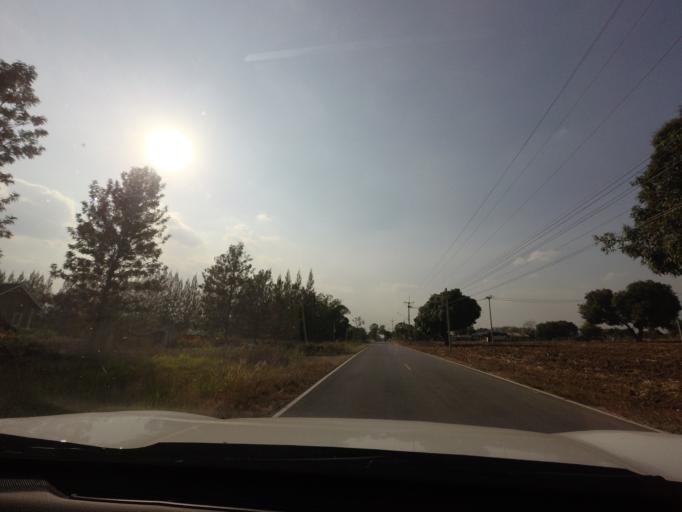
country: TH
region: Nakhon Ratchasima
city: Pak Chong
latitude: 14.6258
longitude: 101.4649
